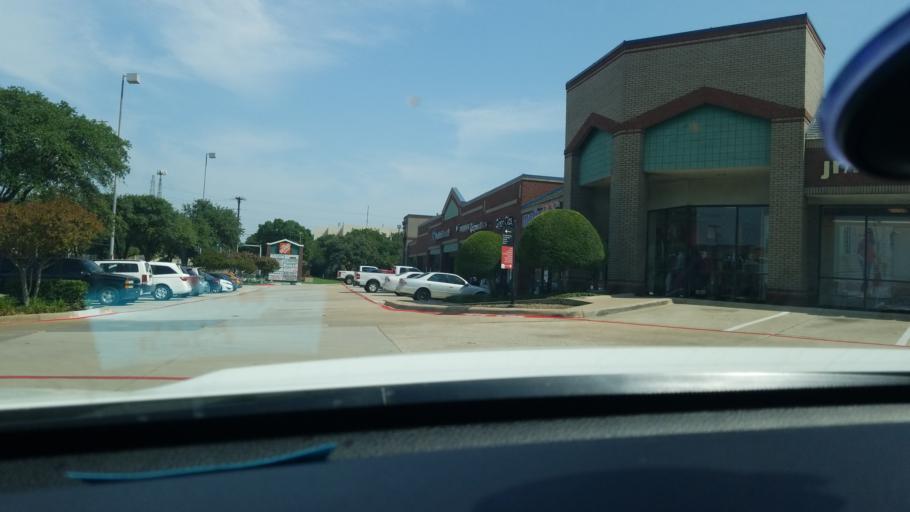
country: US
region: Texas
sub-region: Dallas County
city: Carrollton
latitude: 32.9744
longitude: -96.8896
